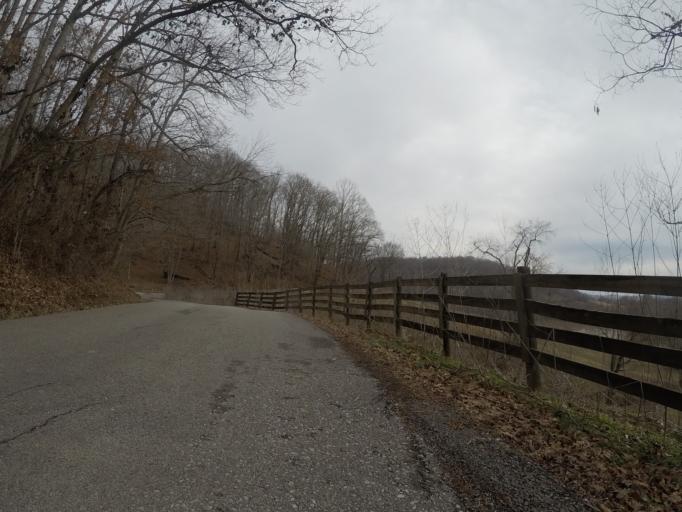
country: US
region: West Virginia
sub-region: Cabell County
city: Huntington
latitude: 38.4389
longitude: -82.4626
